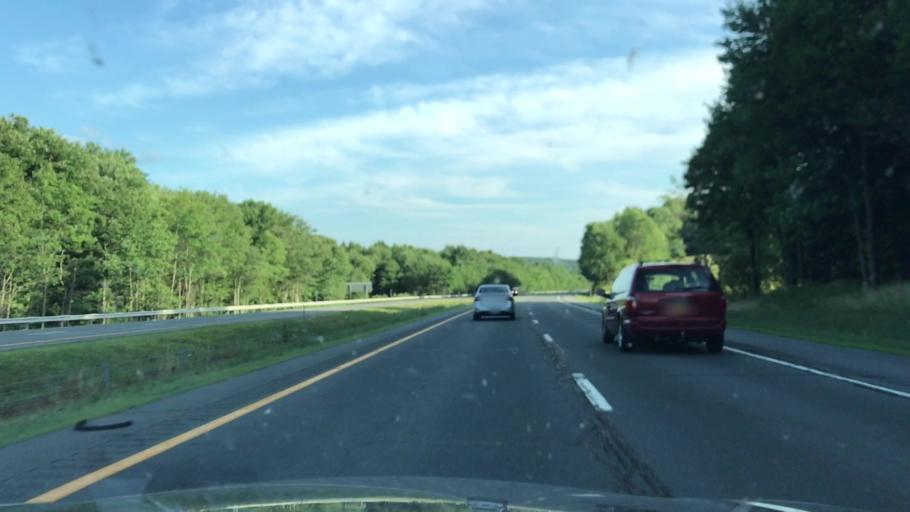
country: US
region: New York
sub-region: Sullivan County
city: Liberty
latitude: 41.7304
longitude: -74.7279
